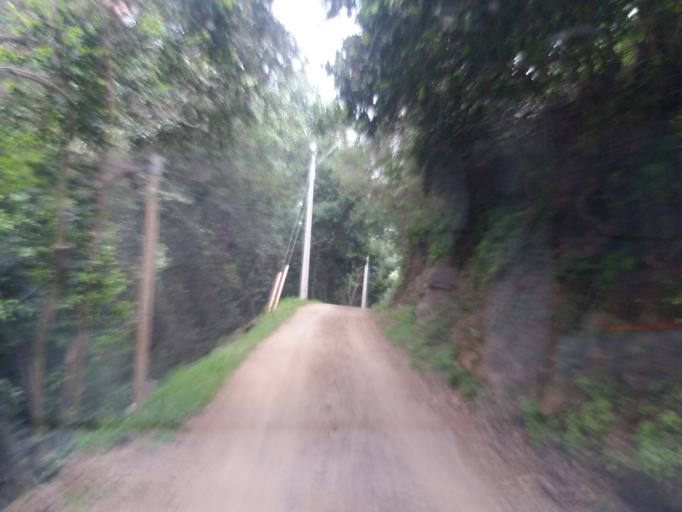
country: CL
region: Valparaiso
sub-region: Provincia de Marga Marga
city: Limache
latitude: -33.0768
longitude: -71.0605
